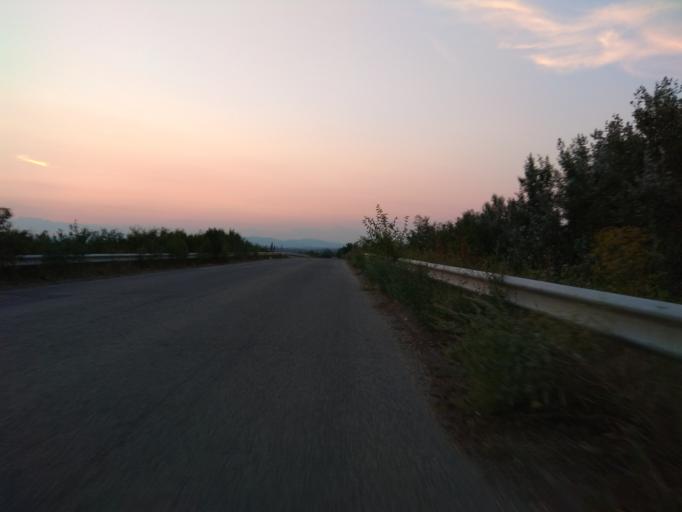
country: HU
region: Borsod-Abauj-Zemplen
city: Emod
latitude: 47.9170
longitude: 20.8454
